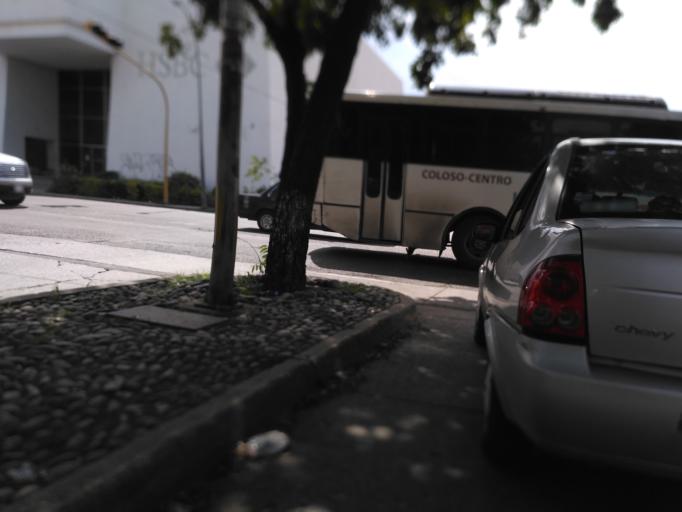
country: MX
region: Sinaloa
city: Culiacan
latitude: 24.7988
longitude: -107.4017
